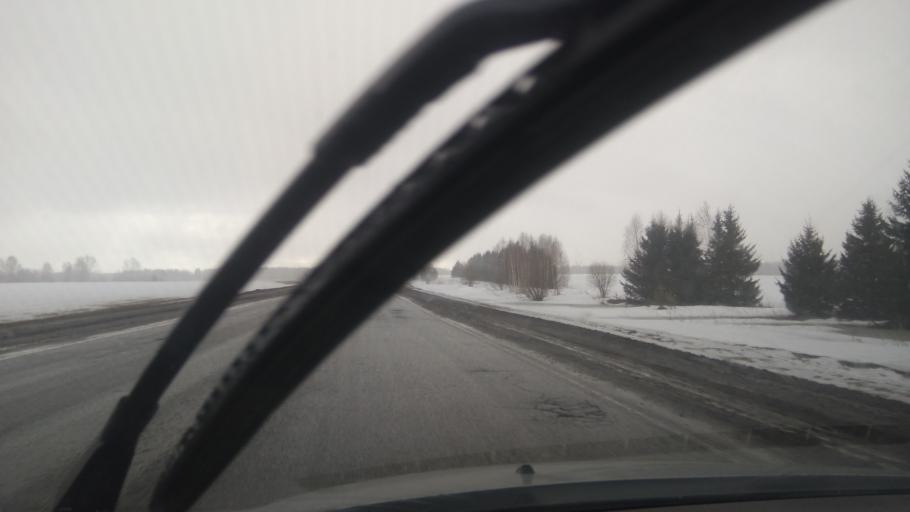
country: RU
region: Perm
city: Orda
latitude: 57.2950
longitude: 56.9892
